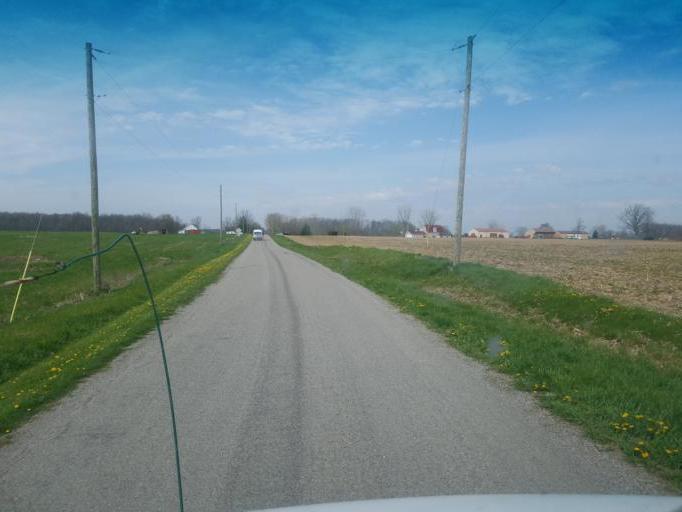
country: US
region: Ohio
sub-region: Union County
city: Richwood
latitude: 40.4855
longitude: -83.4522
